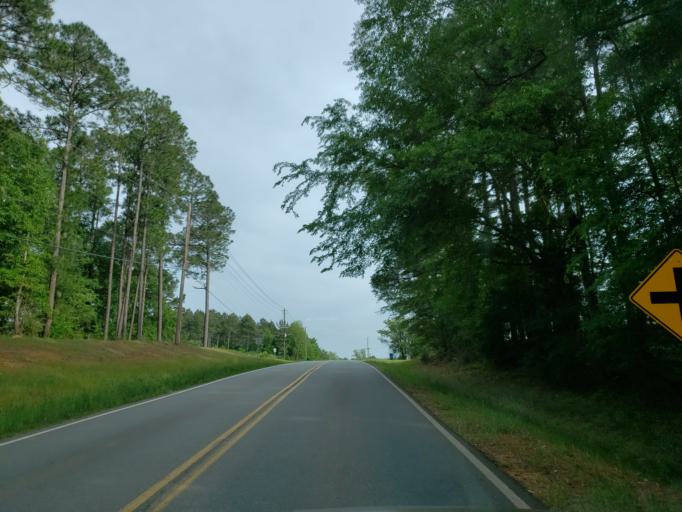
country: US
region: Georgia
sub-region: Dooly County
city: Vienna
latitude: 32.1909
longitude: -83.8985
